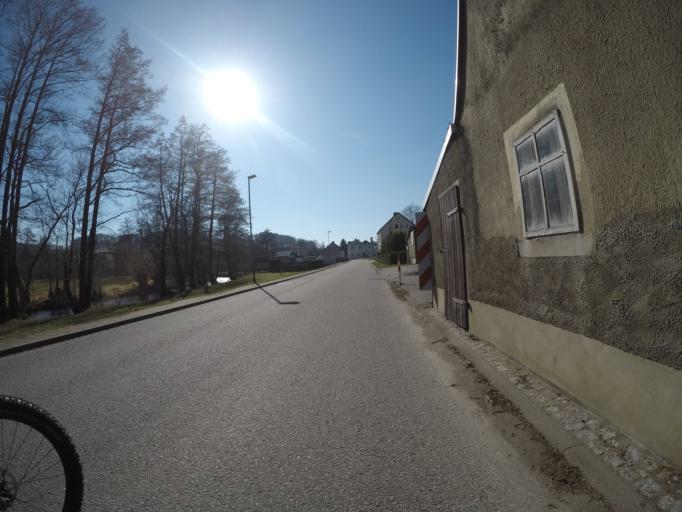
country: DE
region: Saxony
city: Lichtenberg
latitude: 50.8391
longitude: 13.3988
